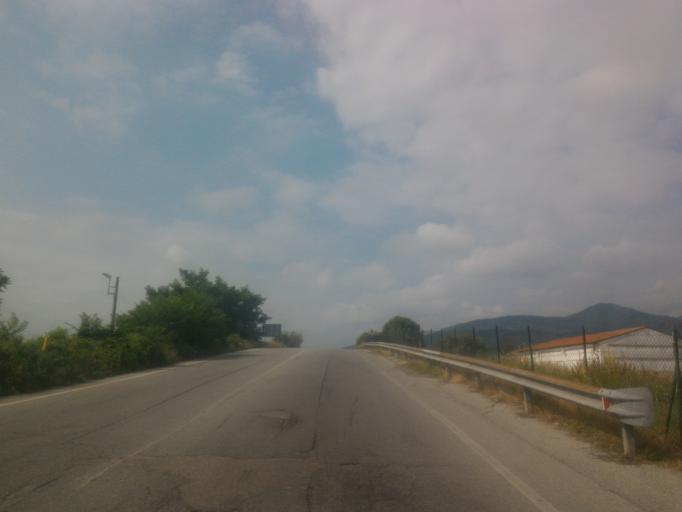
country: IT
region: Piedmont
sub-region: Provincia di Torino
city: Pinerolo
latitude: 44.8801
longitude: 7.3144
